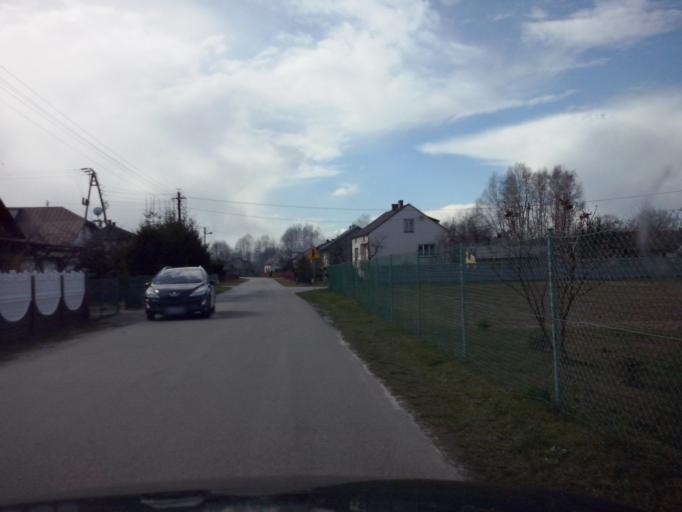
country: PL
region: Subcarpathian Voivodeship
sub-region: Powiat nizanski
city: Bieliny
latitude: 50.4421
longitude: 22.3029
